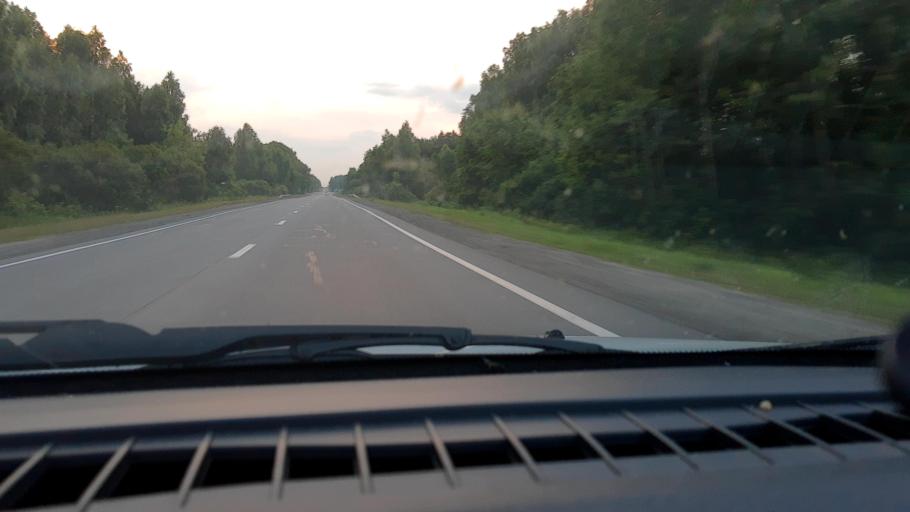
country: RU
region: Nizjnij Novgorod
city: Chernukha
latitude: 55.5623
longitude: 43.9541
